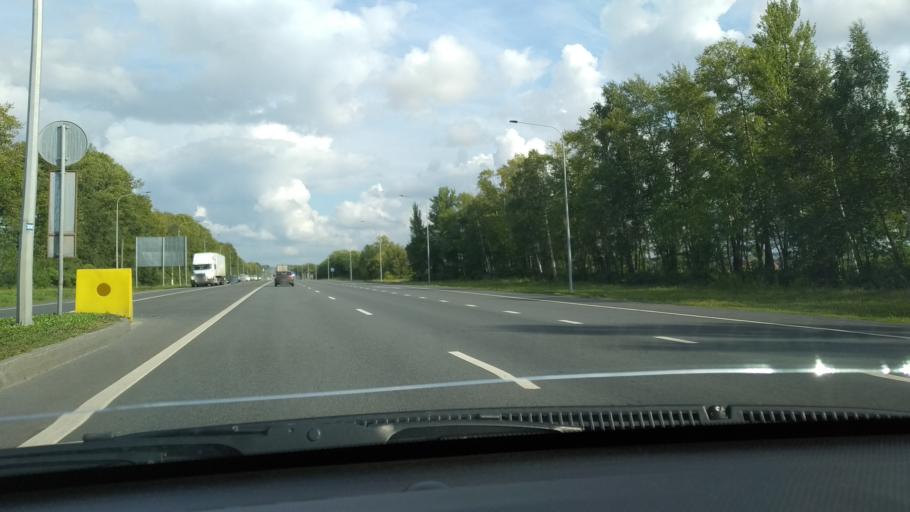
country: RU
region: Tatarstan
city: Stolbishchi
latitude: 55.6599
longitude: 49.3014
